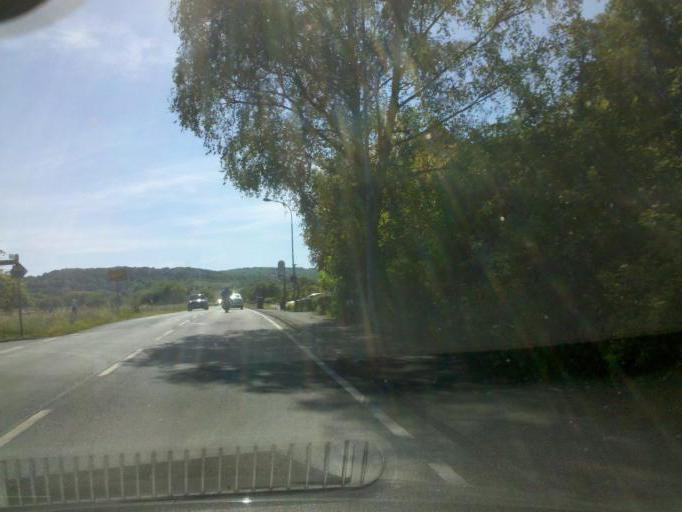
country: DE
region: Hesse
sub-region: Regierungsbezirk Giessen
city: Haiger
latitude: 50.7343
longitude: 8.1951
